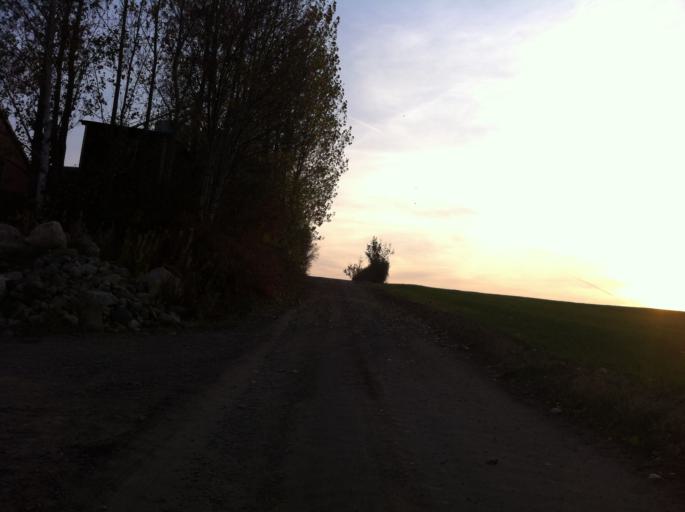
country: SE
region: Skane
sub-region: Svalovs Kommun
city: Teckomatorp
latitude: 55.8652
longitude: 13.0374
